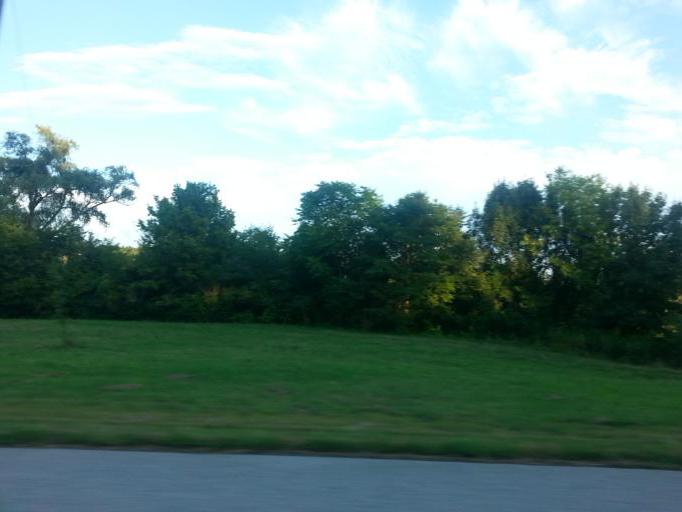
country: US
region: Tennessee
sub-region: Knox County
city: Mascot
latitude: 36.0832
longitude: -83.7639
